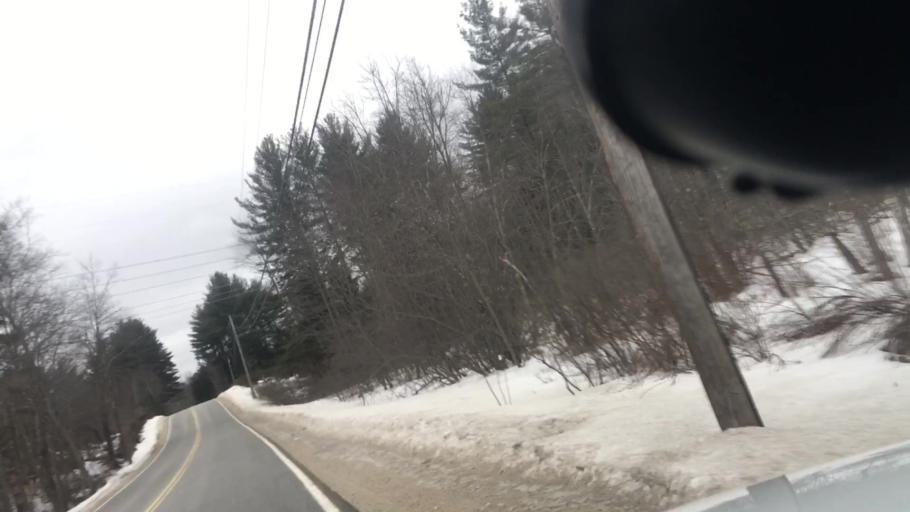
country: US
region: Maine
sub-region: York County
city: Shapleigh
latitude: 43.5111
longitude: -70.8162
